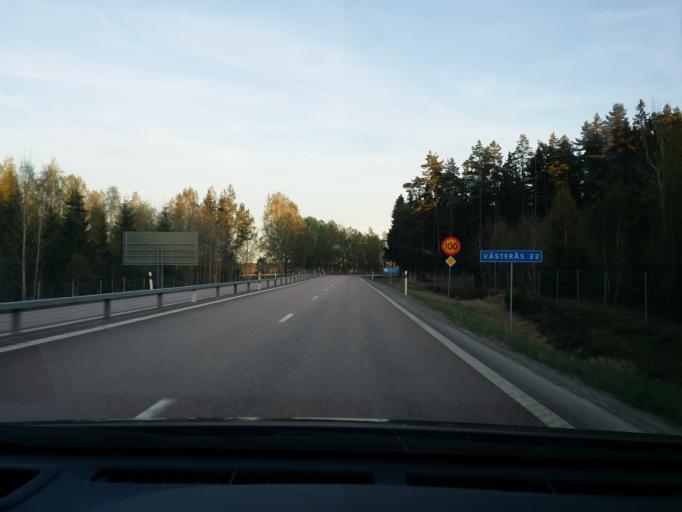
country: SE
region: Vaestmanland
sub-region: Vasteras
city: Tillberga
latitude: 59.7987
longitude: 16.5619
